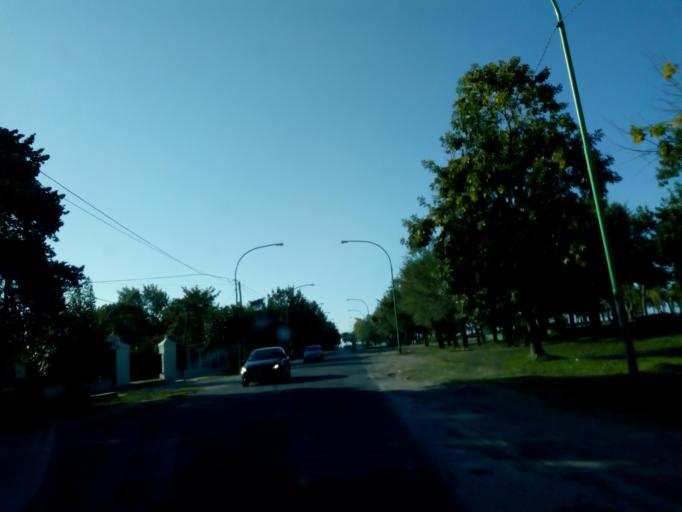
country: AR
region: Buenos Aires
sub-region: Partido de Ensenada
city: Ensenada
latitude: -34.8105
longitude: -57.9811
